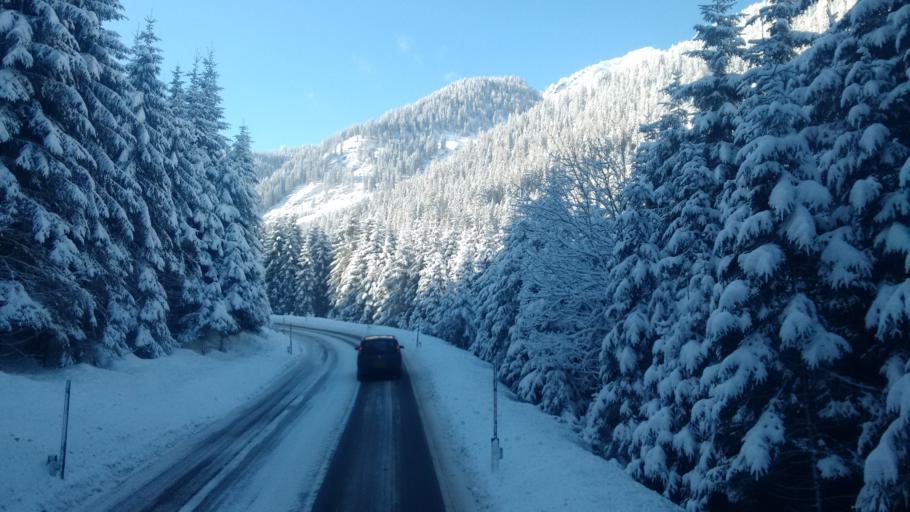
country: AT
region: Salzburg
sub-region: Politischer Bezirk Sankt Johann im Pongau
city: Flachau
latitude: 47.3250
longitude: 13.4449
